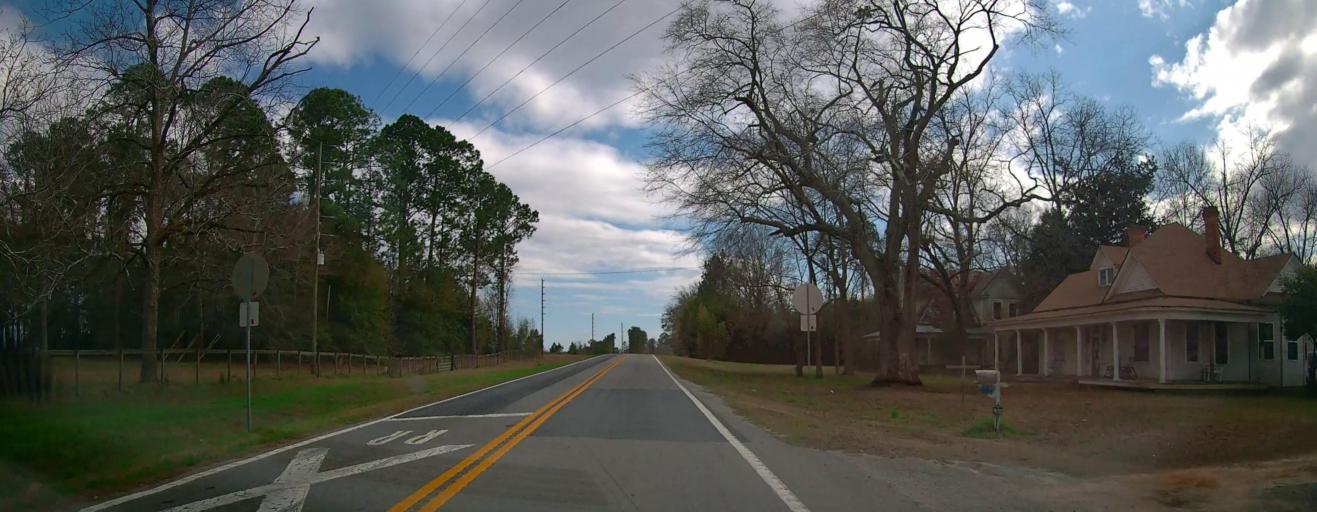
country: US
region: Georgia
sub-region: Taylor County
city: Butler
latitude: 32.4610
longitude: -84.3614
